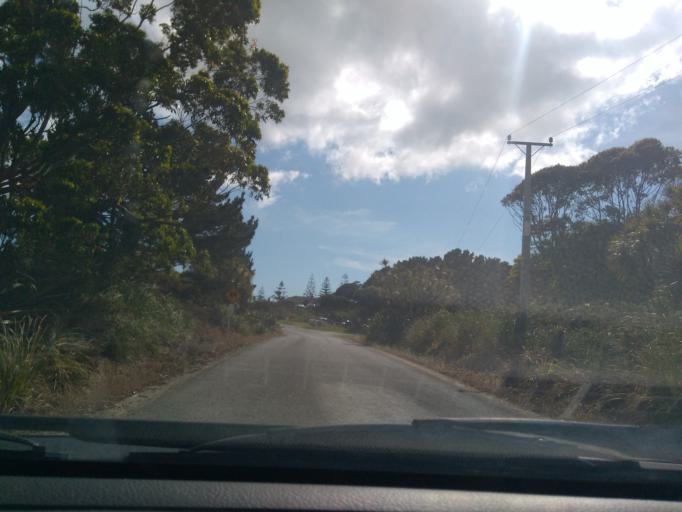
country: NZ
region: Northland
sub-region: Far North District
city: Taipa
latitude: -34.9455
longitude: 173.3807
